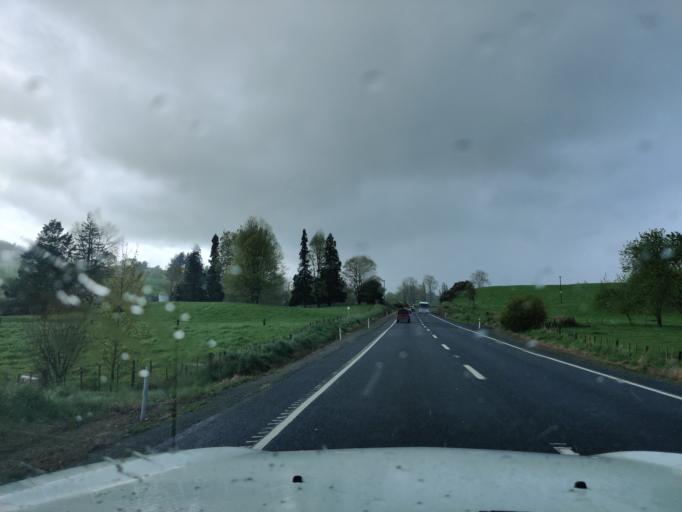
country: NZ
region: Waikato
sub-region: Matamata-Piako District
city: Matamata
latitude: -37.9783
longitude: 175.6999
